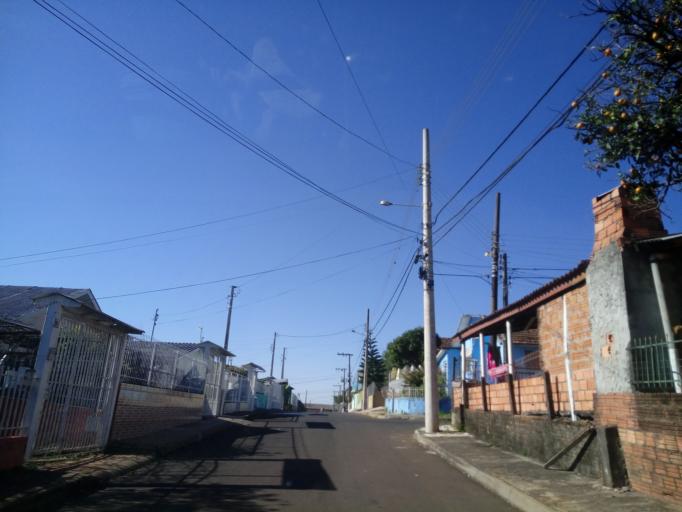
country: BR
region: Santa Catarina
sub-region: Chapeco
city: Chapeco
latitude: -27.0829
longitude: -52.6319
